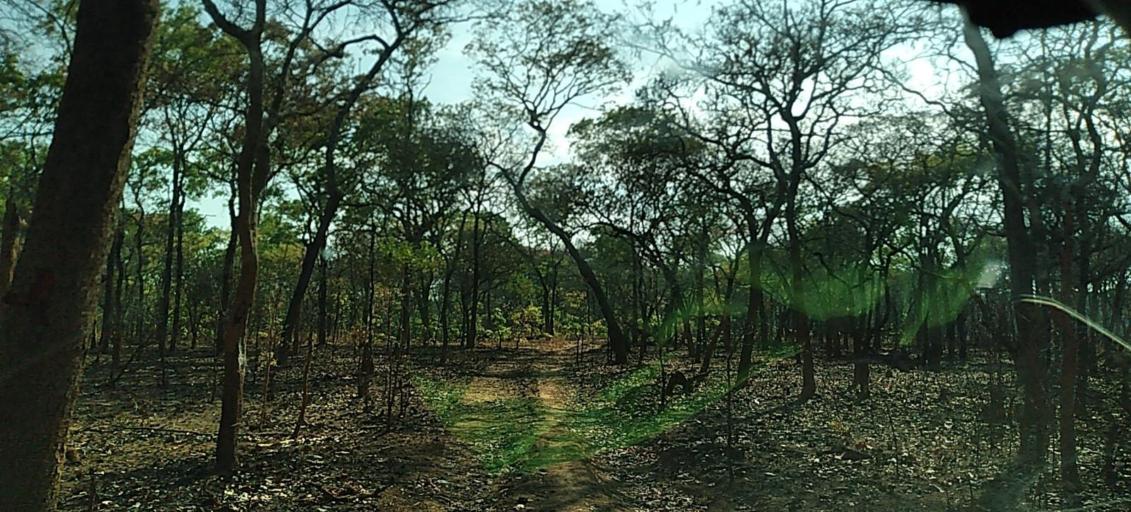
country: ZM
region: North-Western
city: Kalengwa
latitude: -13.2302
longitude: 25.0757
